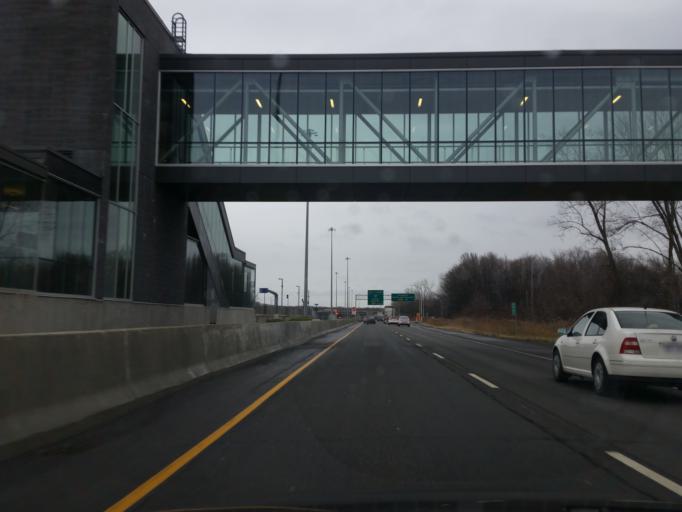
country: CA
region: Quebec
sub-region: Lanaudiere
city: Charlemagne
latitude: 45.7281
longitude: -73.5216
